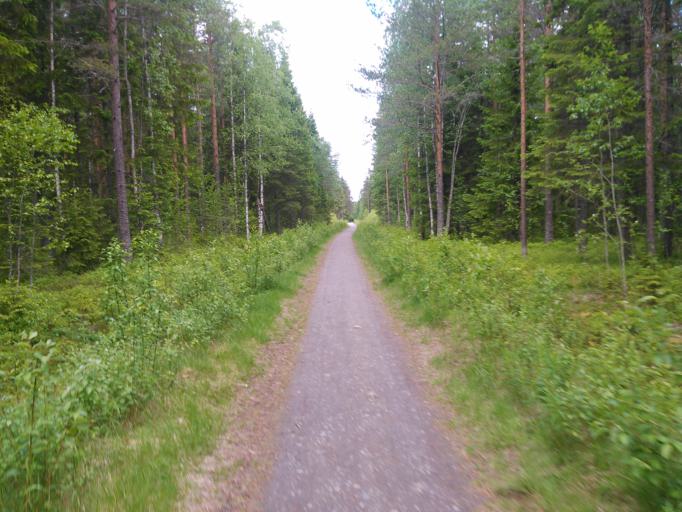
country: SE
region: Vaesterbotten
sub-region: Umea Kommun
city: Ersmark
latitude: 63.8649
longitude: 20.3336
